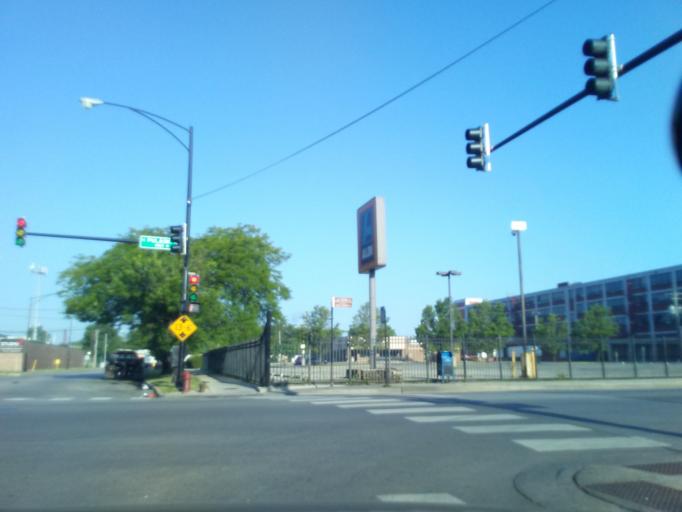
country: US
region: Illinois
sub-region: Cook County
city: Oak Park
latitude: 41.9282
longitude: -87.7268
